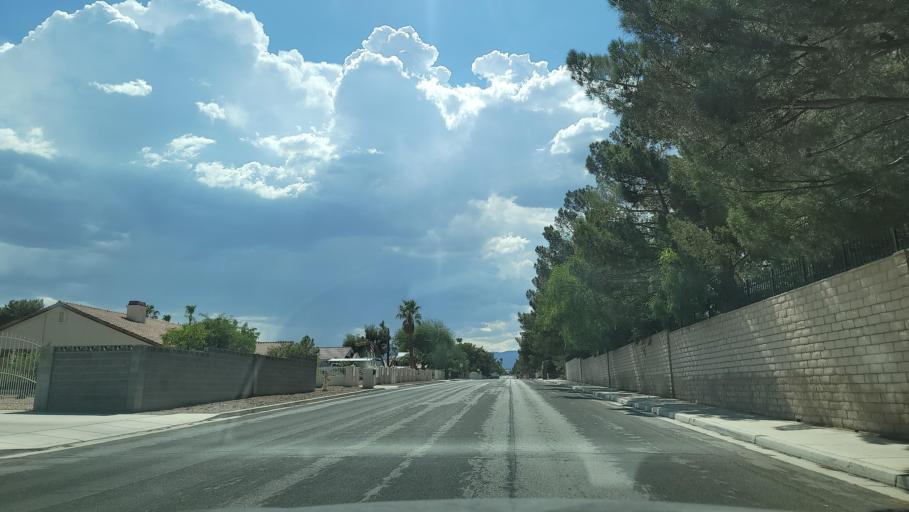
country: US
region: Nevada
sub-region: Clark County
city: Spring Valley
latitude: 36.1312
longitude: -115.2500
